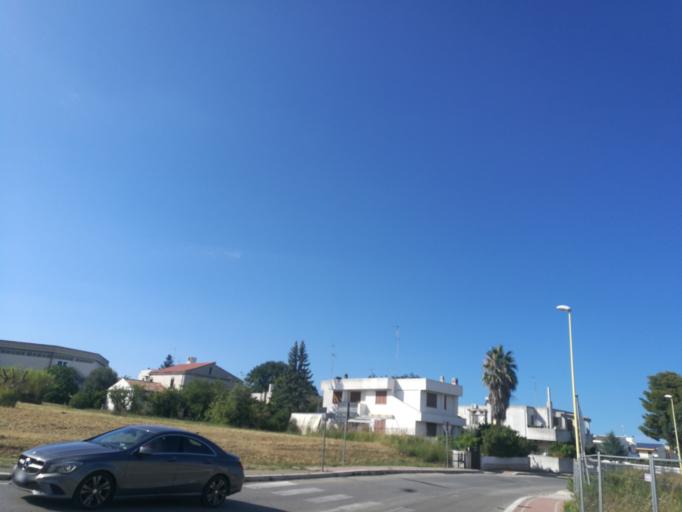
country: IT
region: Molise
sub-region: Provincia di Campobasso
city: Termoli
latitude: 41.9889
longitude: 14.9933
